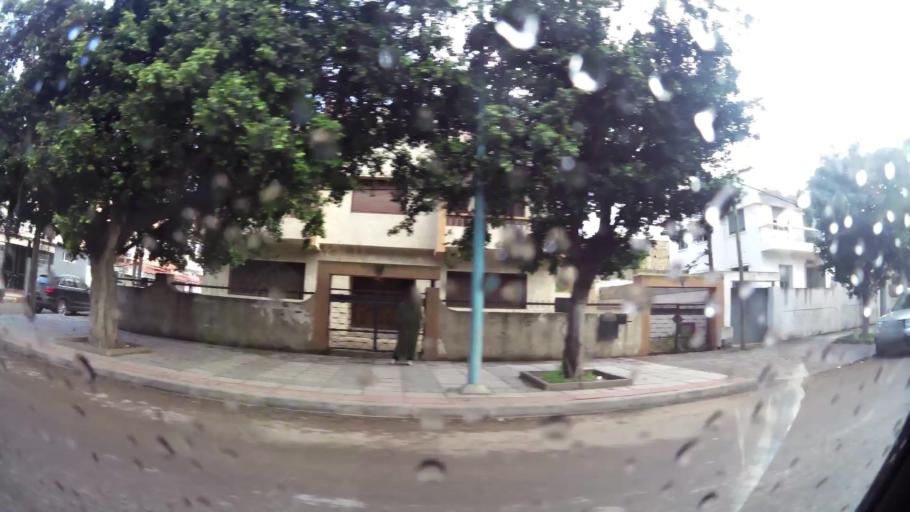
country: MA
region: Doukkala-Abda
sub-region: El-Jadida
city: El Jadida
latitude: 33.2436
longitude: -8.5020
